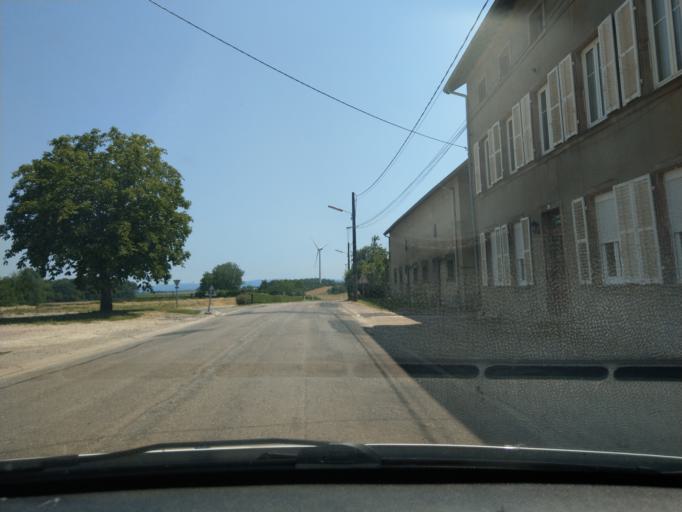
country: FR
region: Lorraine
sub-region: Departement de la Moselle
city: Lorquin
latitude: 48.6329
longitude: 6.8157
